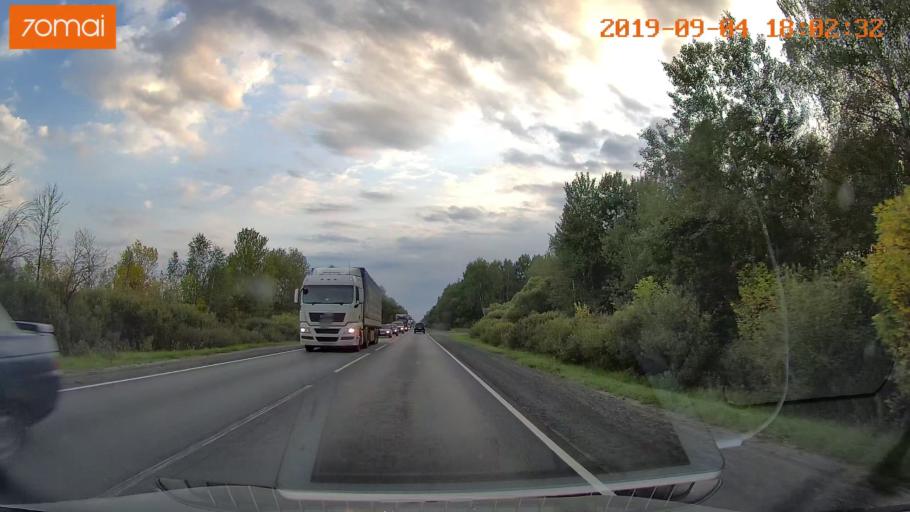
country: RU
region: Moskovskaya
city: Il'inskiy Pogost
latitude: 55.4732
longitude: 38.8636
